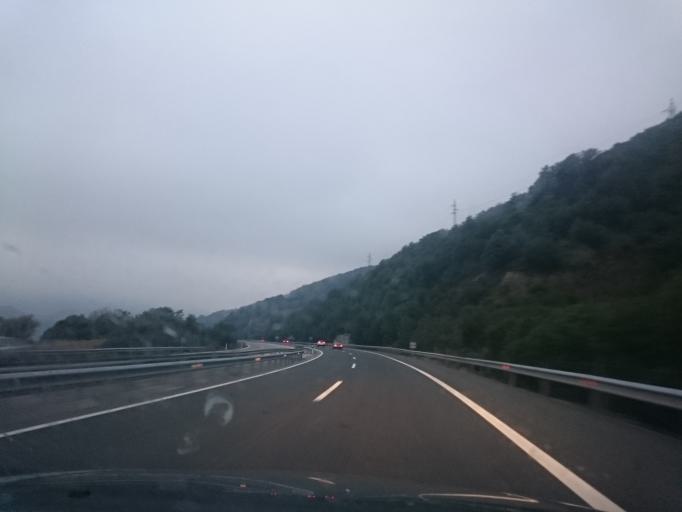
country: ES
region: Asturias
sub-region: Province of Asturias
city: Pola de Lena
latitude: 43.0402
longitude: -5.8194
